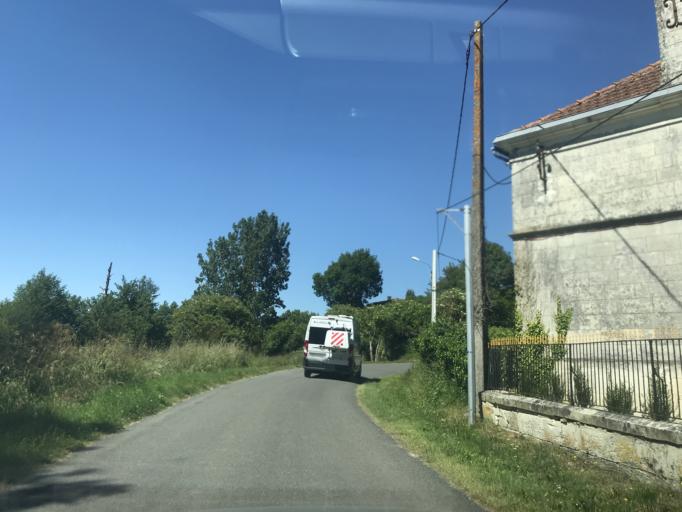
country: FR
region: Poitou-Charentes
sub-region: Departement de la Charente-Maritime
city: Mortagne-sur-Gironde
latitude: 45.4264
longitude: -0.7378
